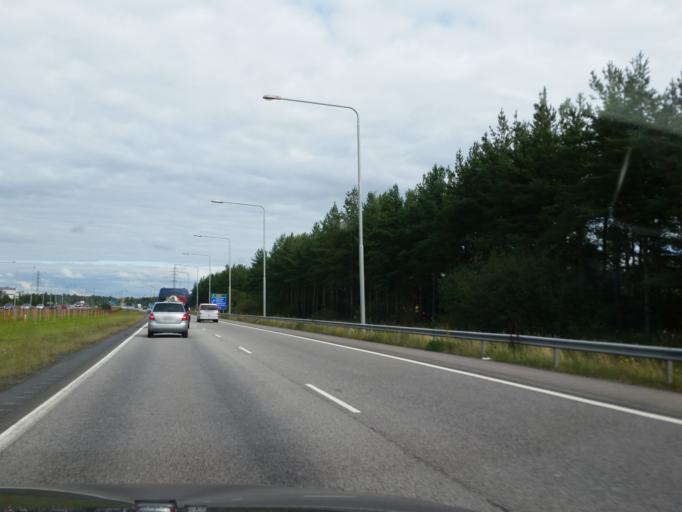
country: FI
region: Uusimaa
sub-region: Helsinki
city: Vantaa
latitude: 60.2622
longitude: 24.9655
